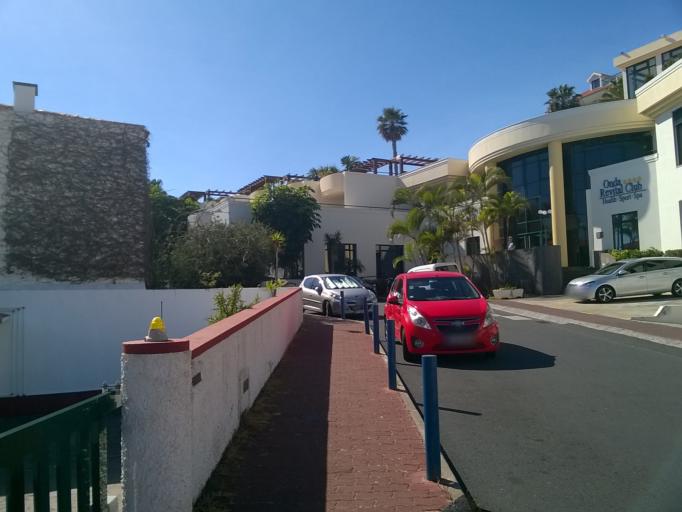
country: PT
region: Madeira
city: Canico
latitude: 32.6423
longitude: -16.8312
